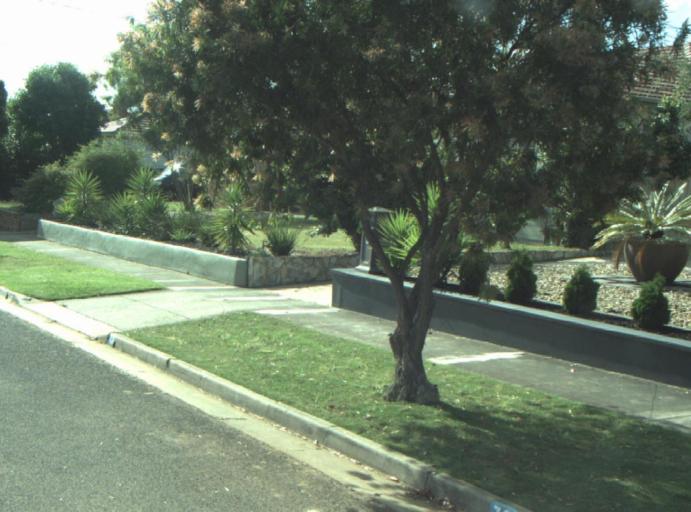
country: AU
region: Victoria
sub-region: Greater Geelong
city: Wandana Heights
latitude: -38.1724
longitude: 144.3338
